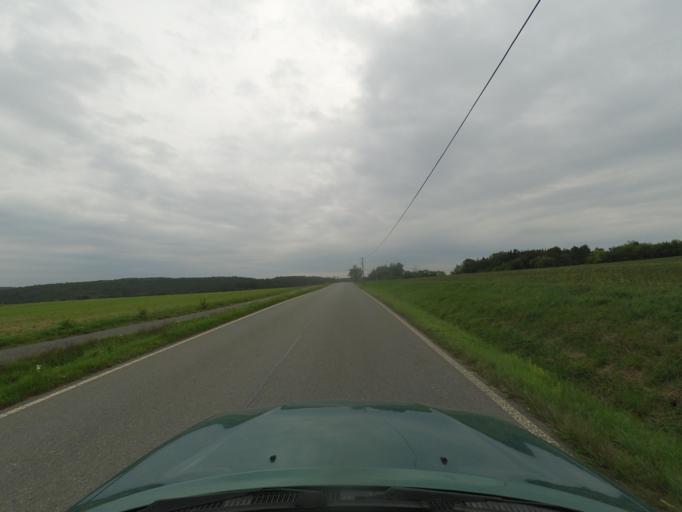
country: CZ
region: Plzensky
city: Stankov
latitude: 49.5478
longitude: 13.0879
